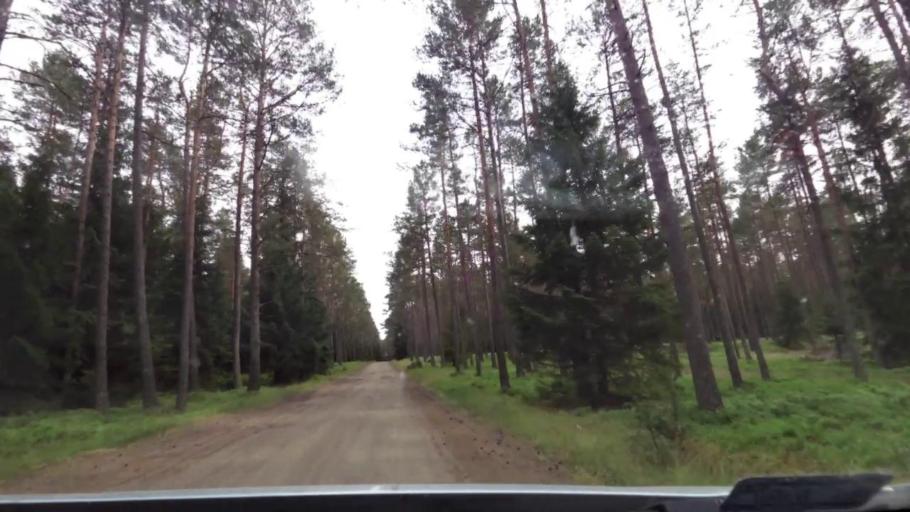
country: PL
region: Pomeranian Voivodeship
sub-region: Powiat bytowski
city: Trzebielino
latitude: 54.2144
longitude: 17.0040
